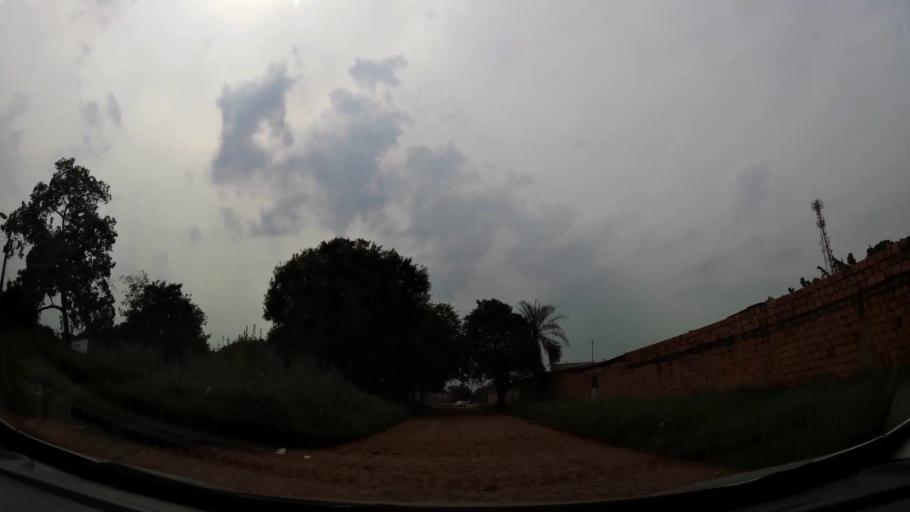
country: PY
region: Alto Parana
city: Presidente Franco
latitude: -25.5419
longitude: -54.6429
